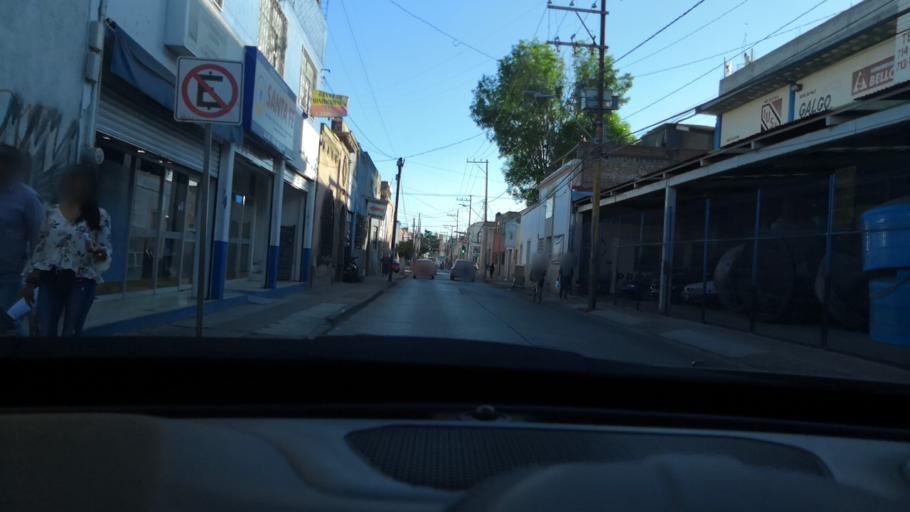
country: MX
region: Guanajuato
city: Leon
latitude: 21.1299
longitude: -101.6810
